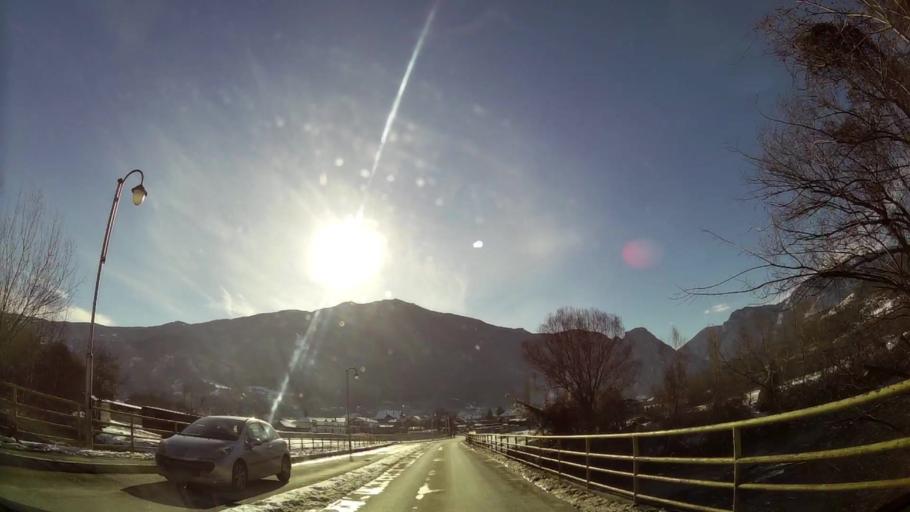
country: MK
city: Ljubin
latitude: 41.9808
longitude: 21.3086
